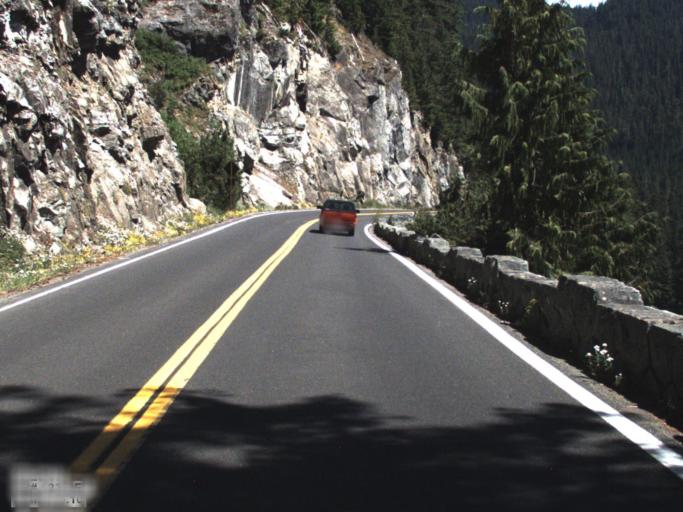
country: US
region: Washington
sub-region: King County
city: Enumclaw
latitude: 46.8560
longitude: -121.5268
